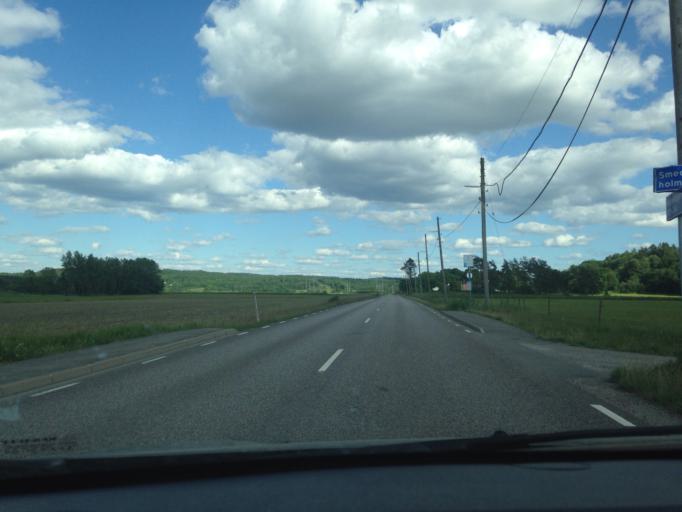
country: SE
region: Vaestra Goetaland
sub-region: Goteborg
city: Majorna
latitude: 57.7727
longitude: 11.9154
